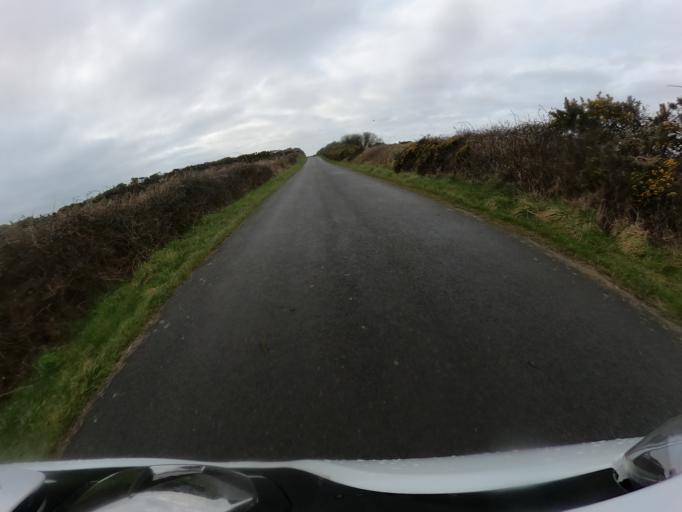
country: IM
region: Ramsey
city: Ramsey
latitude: 54.3494
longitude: -4.5240
